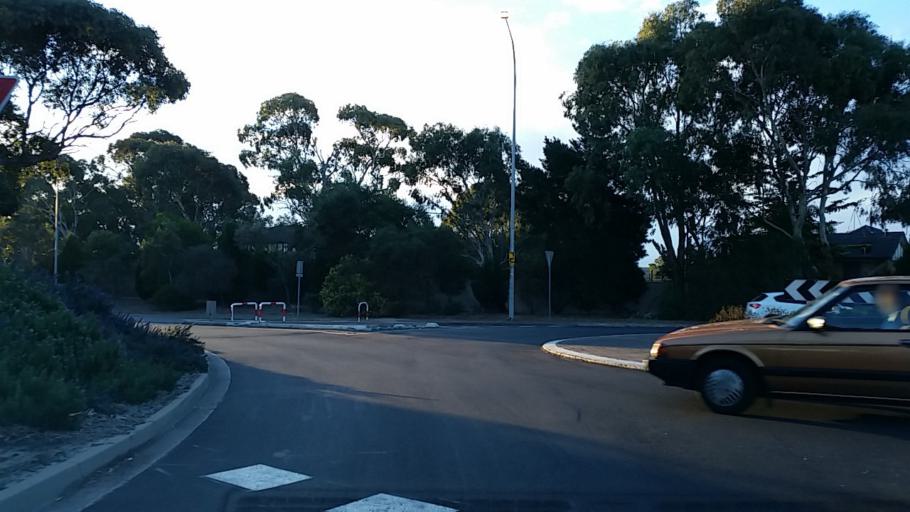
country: AU
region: South Australia
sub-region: Onkaparinga
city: Craigburn Farm
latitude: -35.0589
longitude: 138.6035
